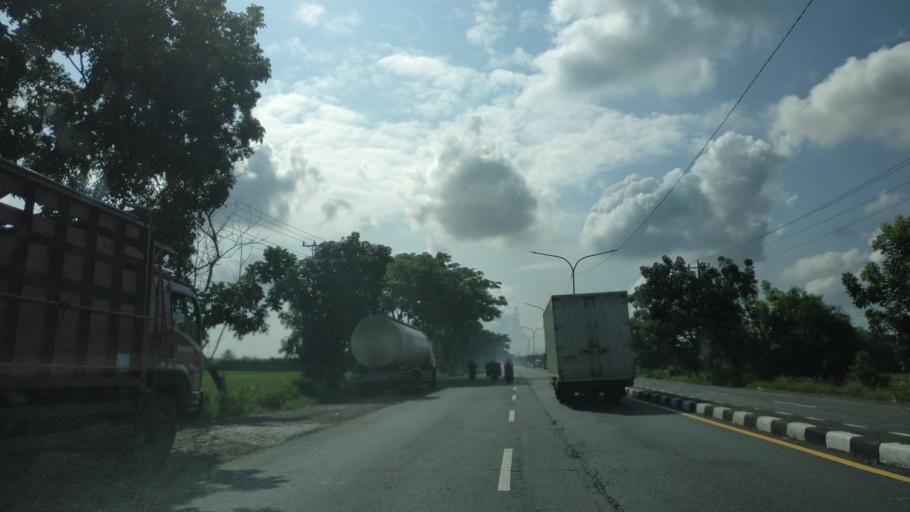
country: ID
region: Central Java
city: Comal
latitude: -6.9006
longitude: 109.5018
